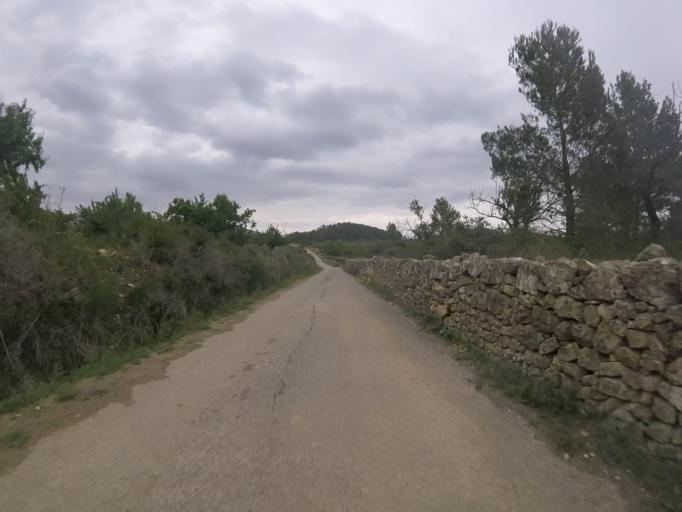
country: ES
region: Valencia
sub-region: Provincia de Castello
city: Sarratella
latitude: 40.2711
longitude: 0.0709
